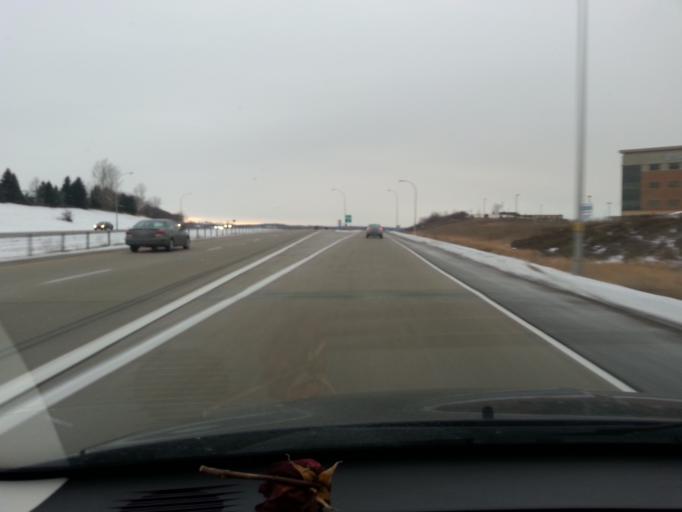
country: US
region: Minnesota
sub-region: Dakota County
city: Burnsville
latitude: 44.7474
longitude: -93.2715
